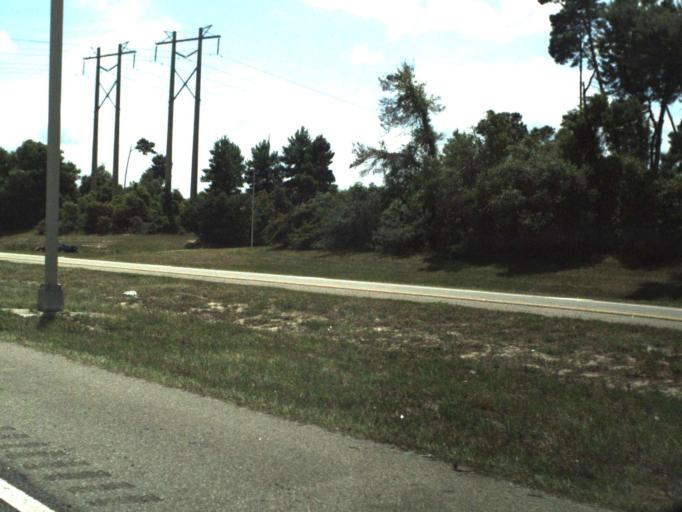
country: US
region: Florida
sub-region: Volusia County
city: Deltona
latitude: 28.9133
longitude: -81.2712
